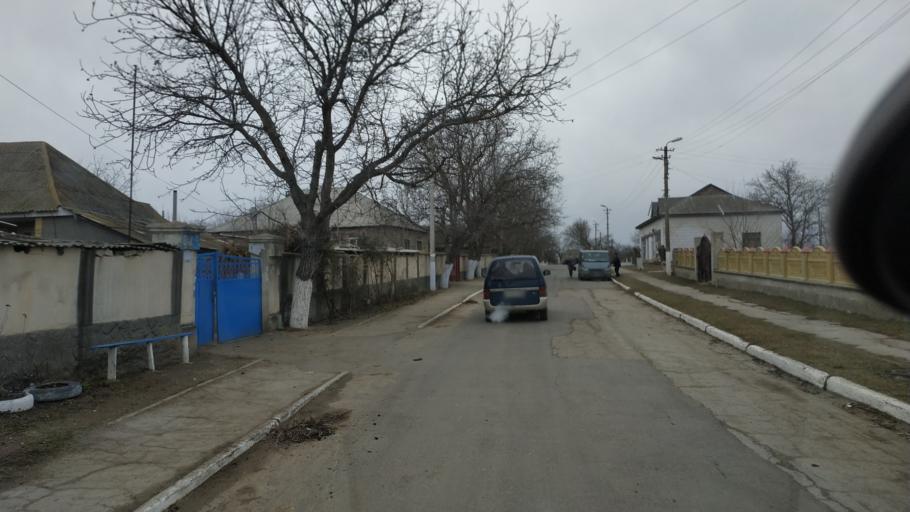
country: MD
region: Telenesti
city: Cocieri
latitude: 47.2573
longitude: 29.0623
